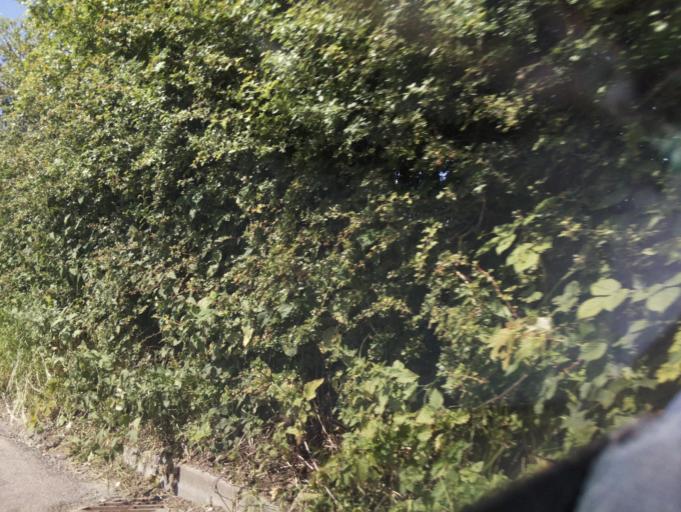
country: GB
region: England
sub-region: Derbyshire
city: Buxton
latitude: 53.1940
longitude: -1.8781
